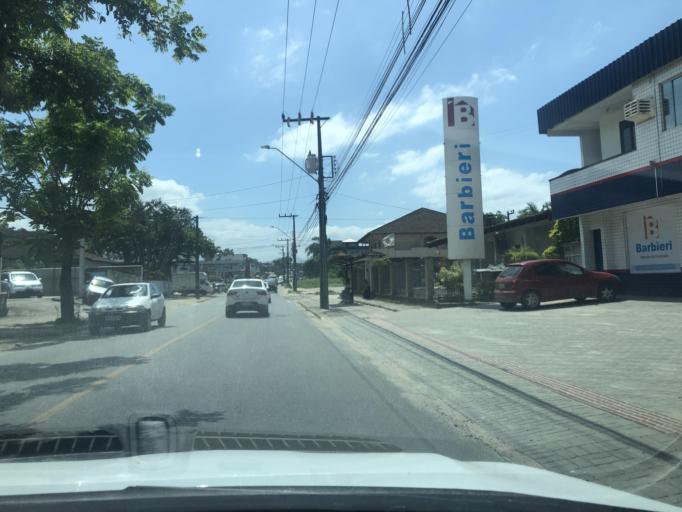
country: BR
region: Santa Catarina
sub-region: Joinville
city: Joinville
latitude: -26.3323
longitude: -48.8215
